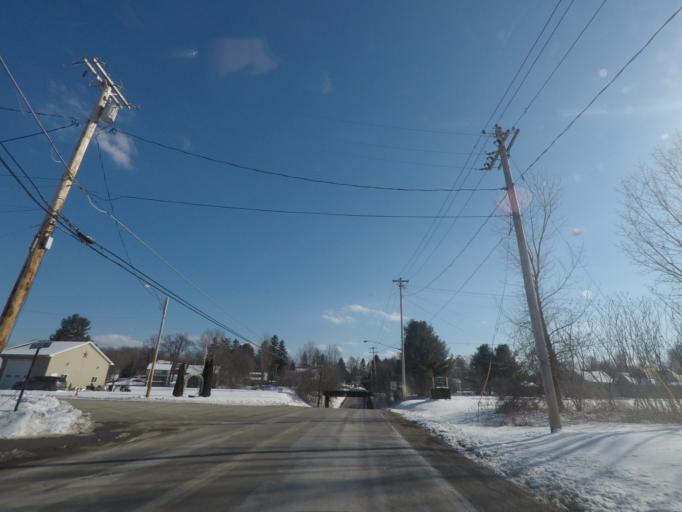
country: US
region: New York
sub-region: Saratoga County
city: Stillwater
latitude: 42.9164
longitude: -73.5142
